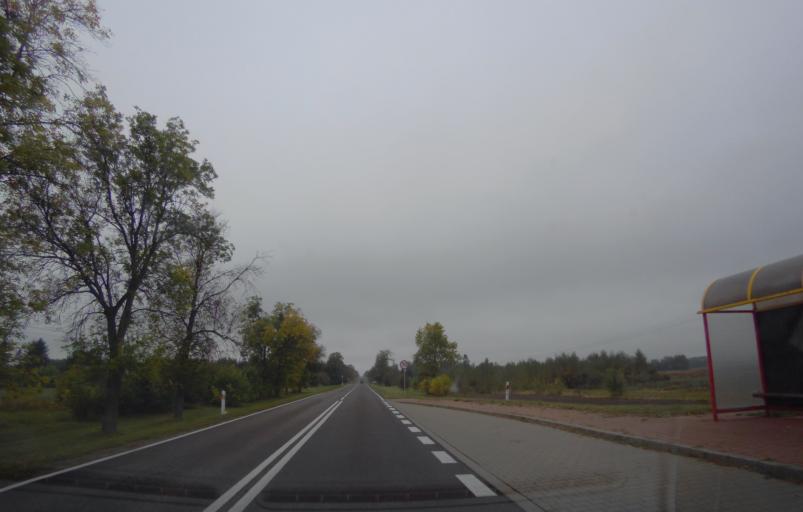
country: PL
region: Lublin Voivodeship
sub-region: Chelm
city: Chelm
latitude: 51.1882
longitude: 23.4357
